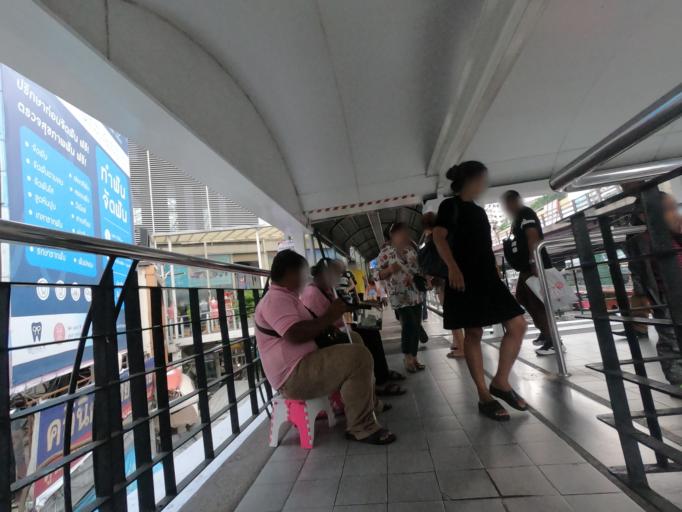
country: TH
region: Bangkok
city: Bang Kapi
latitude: 13.7576
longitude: 100.6412
